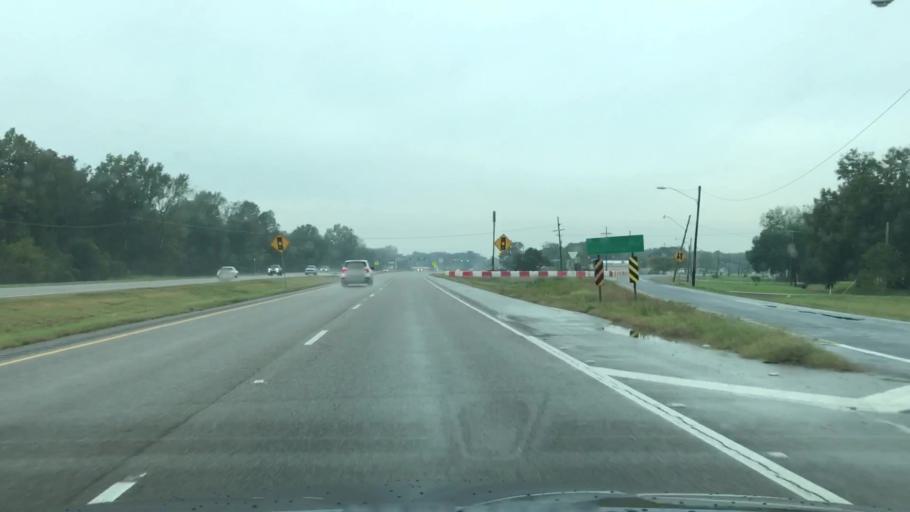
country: US
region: Louisiana
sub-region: Saint Charles Parish
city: Des Allemands
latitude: 29.8269
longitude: -90.4620
